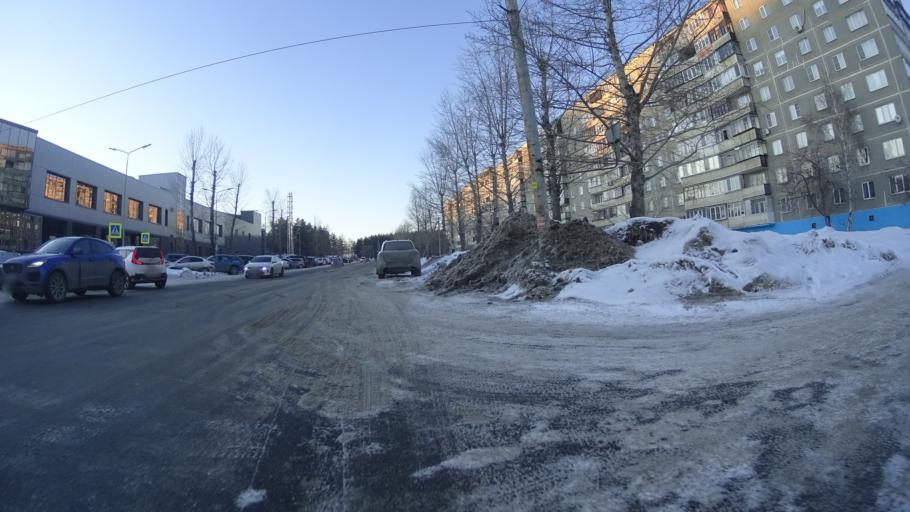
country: RU
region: Chelyabinsk
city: Roshchino
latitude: 55.1949
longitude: 61.3000
